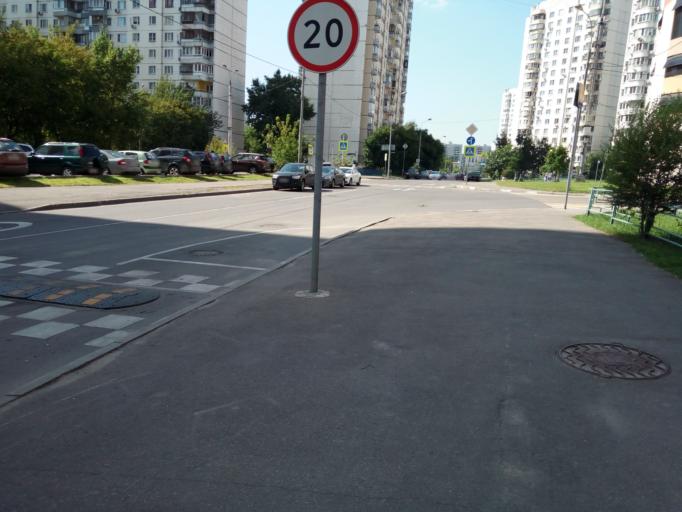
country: RU
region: Moscow
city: Sokol
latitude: 55.7794
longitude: 37.5325
